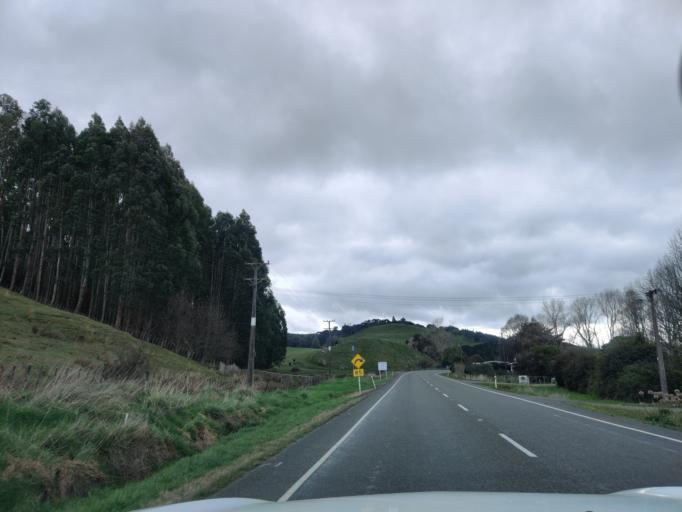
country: NZ
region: Manawatu-Wanganui
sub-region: Rangitikei District
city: Bulls
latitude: -39.9302
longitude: 175.5768
